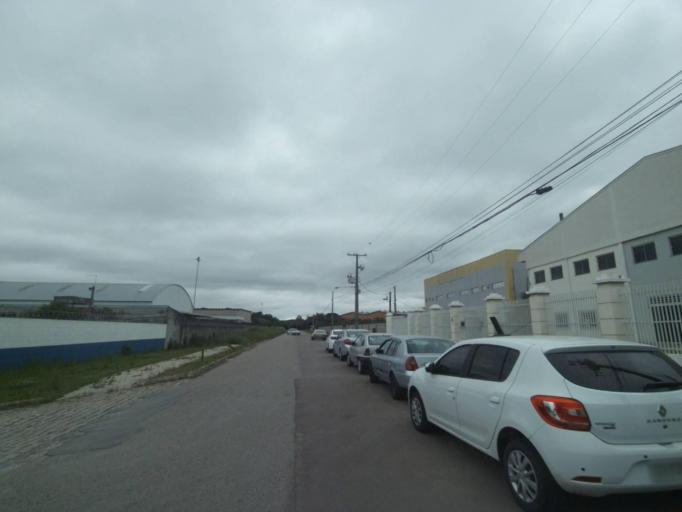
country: BR
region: Parana
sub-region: Curitiba
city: Curitiba
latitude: -25.5207
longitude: -49.3243
